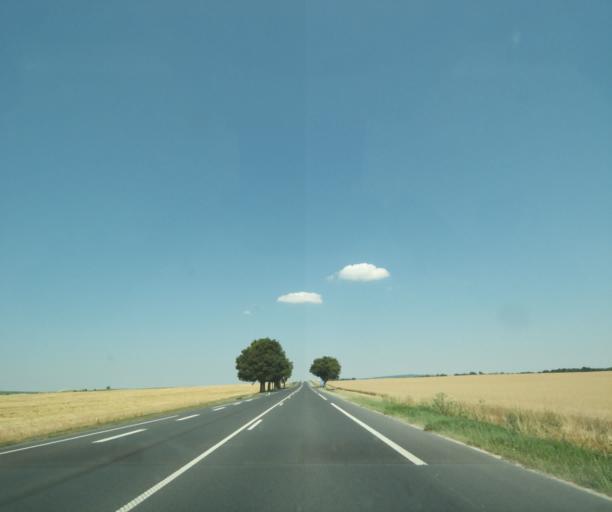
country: FR
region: Champagne-Ardenne
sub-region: Departement de la Marne
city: Verzy
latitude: 49.1535
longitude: 4.2091
